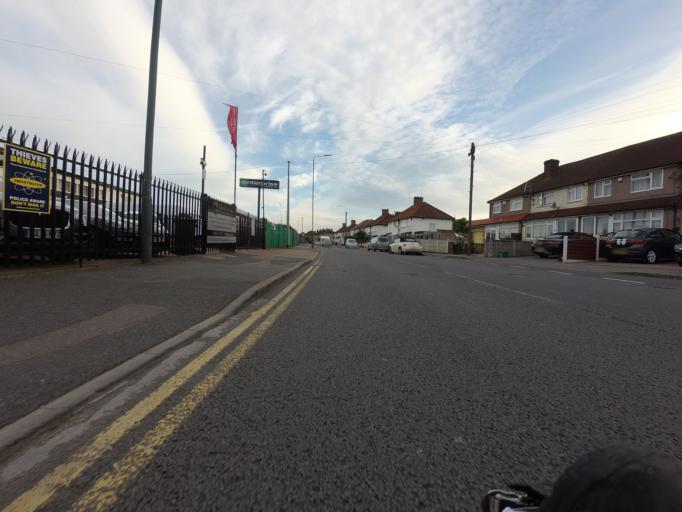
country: GB
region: England
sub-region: Greater London
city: Sidcup
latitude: 51.4169
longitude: 0.1158
